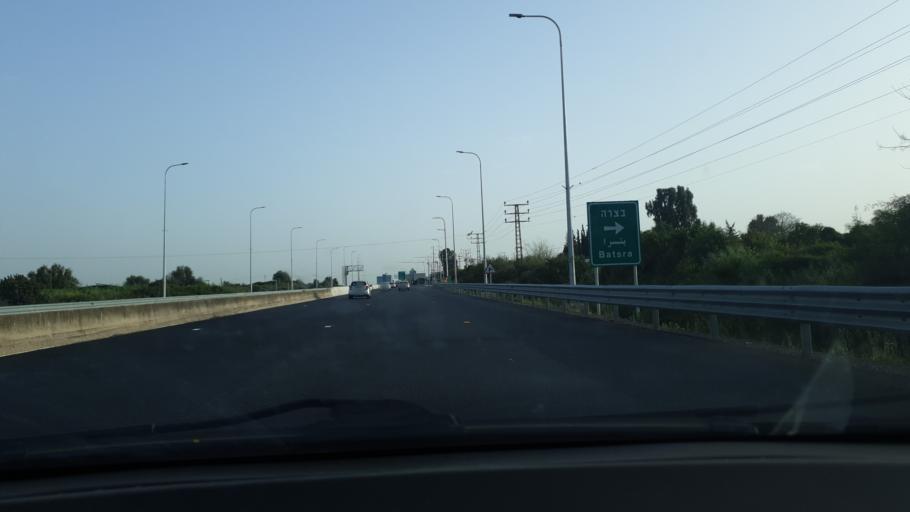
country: IL
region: Central District
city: Ra'anana
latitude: 32.2126
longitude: 34.8835
